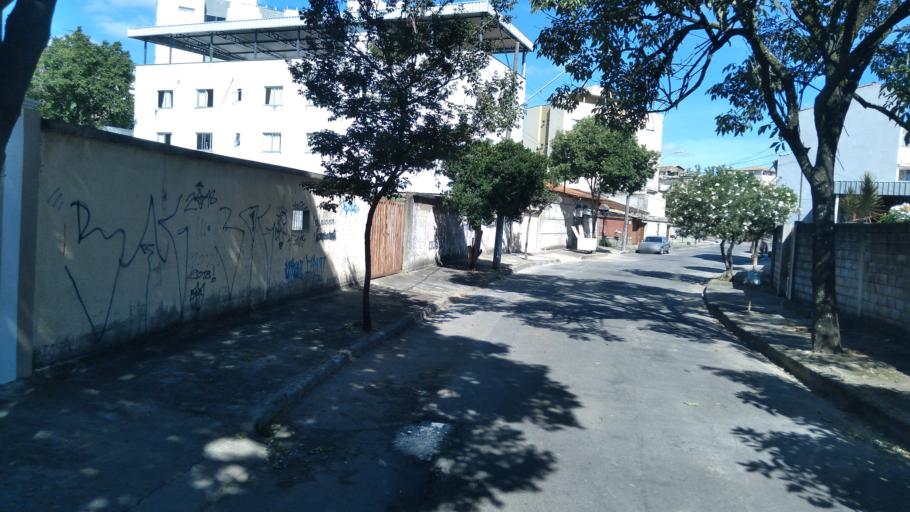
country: BR
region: Minas Gerais
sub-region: Belo Horizonte
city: Belo Horizonte
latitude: -19.8563
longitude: -43.9130
